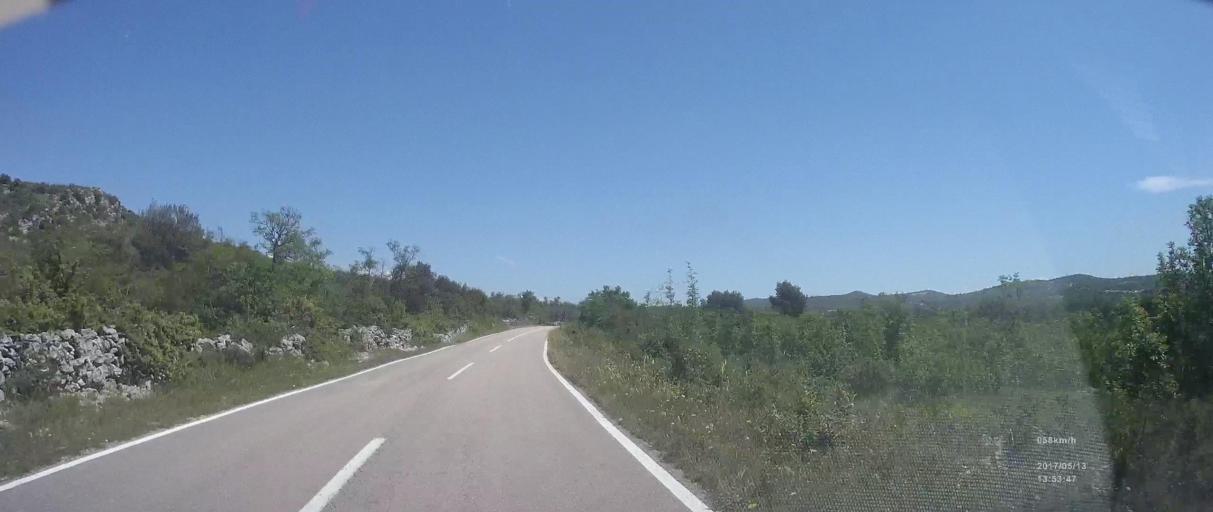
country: HR
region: Sibensko-Kniniska
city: Primosten
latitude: 43.5980
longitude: 16.0015
